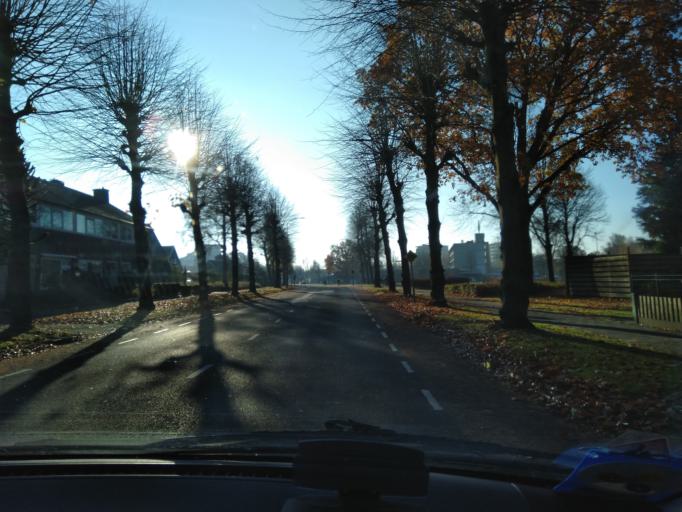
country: NL
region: Drenthe
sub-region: Gemeente Assen
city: Assen
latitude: 53.0030
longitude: 6.5485
